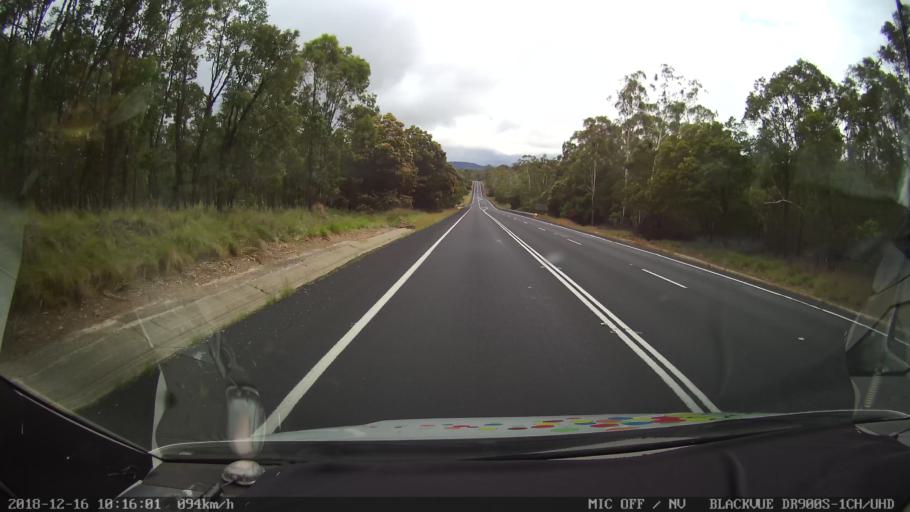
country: AU
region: New South Wales
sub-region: Tenterfield Municipality
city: Carrolls Creek
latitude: -29.2712
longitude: 151.9782
